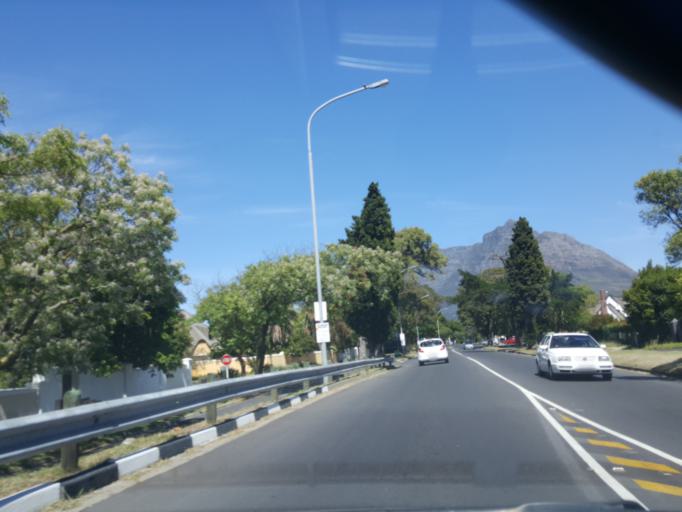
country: ZA
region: Western Cape
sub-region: City of Cape Town
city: Rosebank
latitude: -33.9420
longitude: 18.4992
